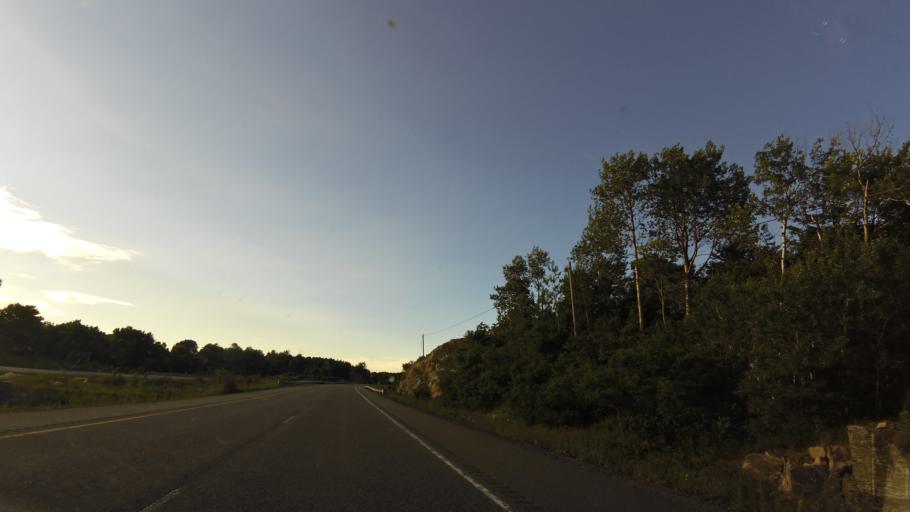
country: CA
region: Ontario
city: Midland
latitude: 44.8356
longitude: -79.7386
